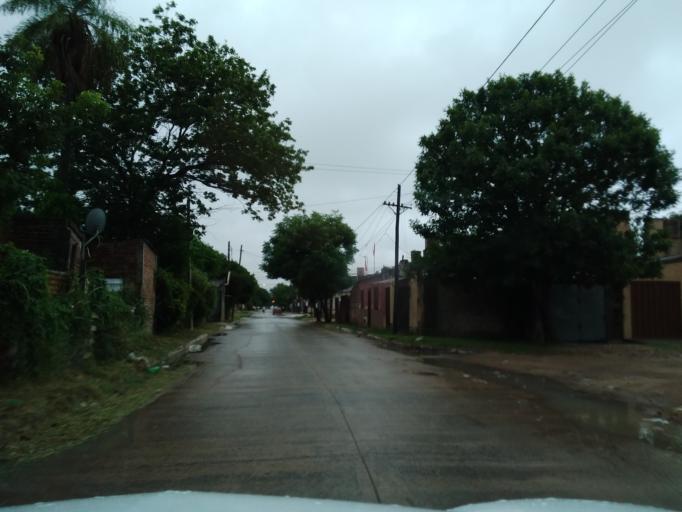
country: AR
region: Corrientes
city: Corrientes
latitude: -27.4833
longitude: -58.8242
